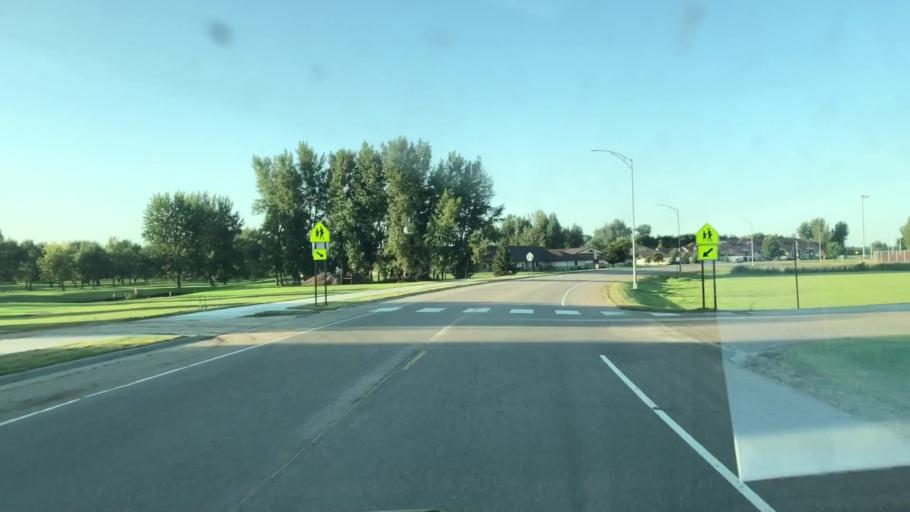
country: US
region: Minnesota
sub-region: Nobles County
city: Worthington
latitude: 43.6285
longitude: -95.6287
